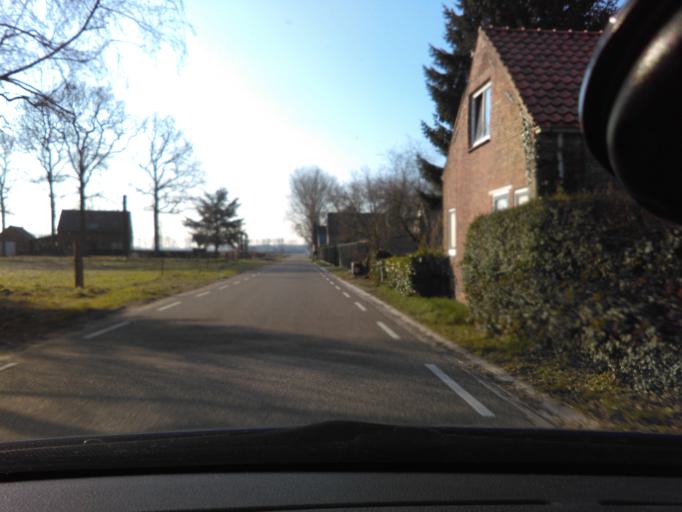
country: NL
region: Zeeland
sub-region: Gemeente Terneuzen
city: Koewacht
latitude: 51.2614
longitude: 3.9822
